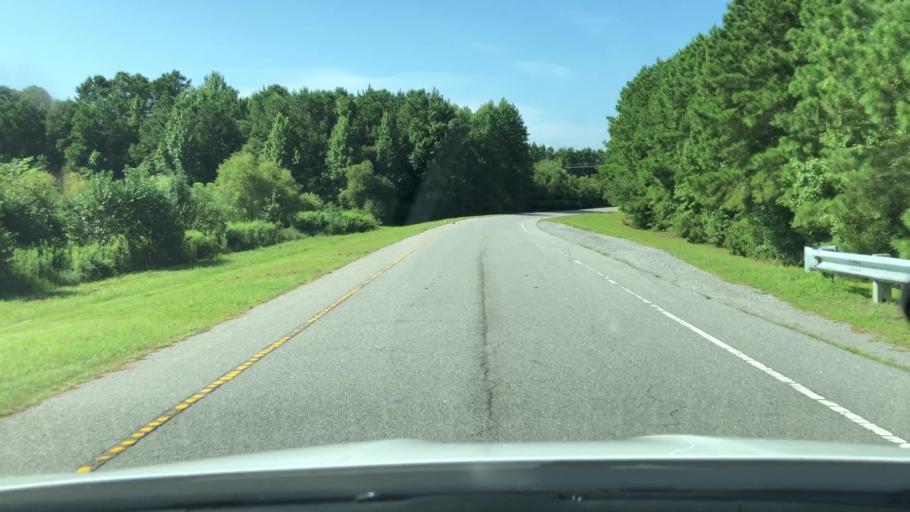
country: US
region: North Carolina
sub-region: Chowan County
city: Edenton
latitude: 36.0606
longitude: -76.6709
